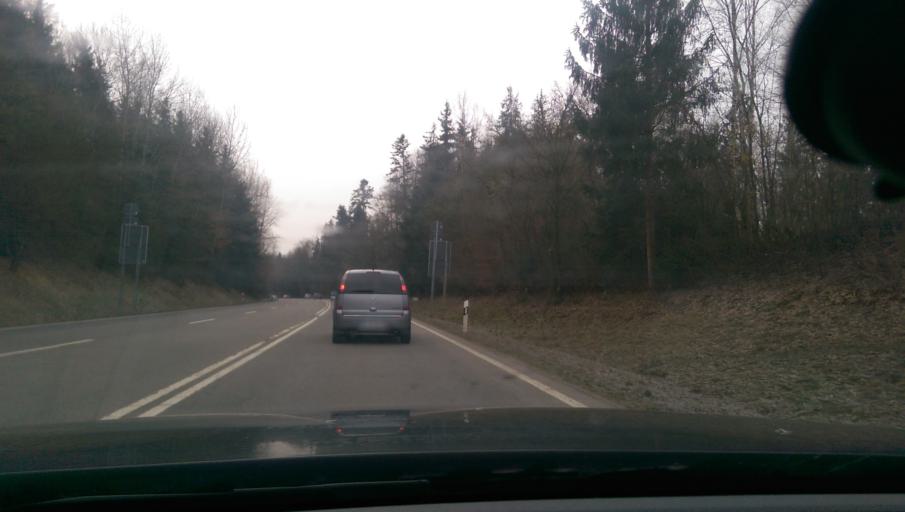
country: DE
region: Bavaria
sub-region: Lower Bavaria
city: Passau
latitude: 48.5859
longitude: 13.4175
